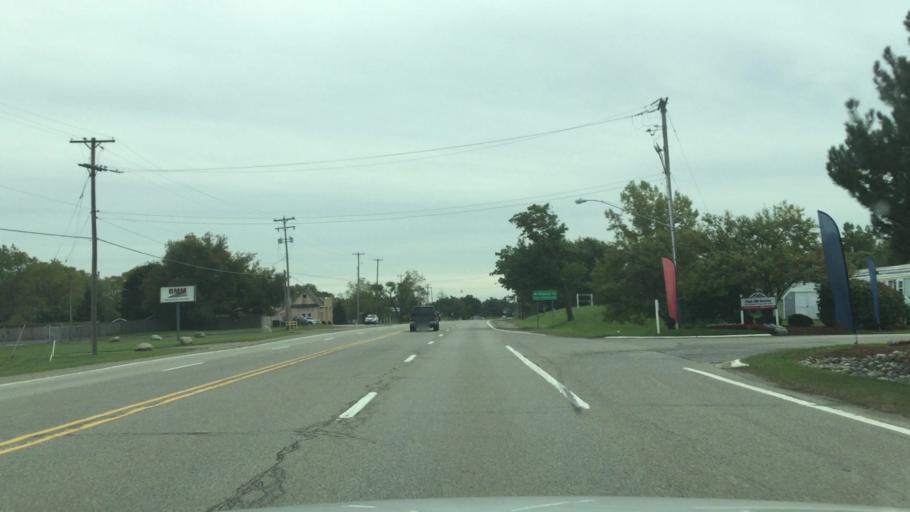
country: US
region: Michigan
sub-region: Oakland County
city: Ortonville
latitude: 42.7903
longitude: -83.5114
